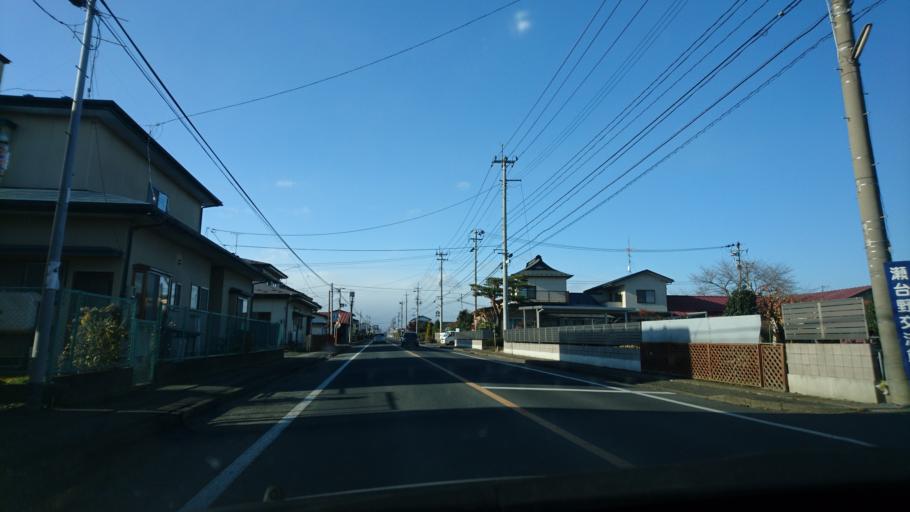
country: JP
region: Iwate
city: Mizusawa
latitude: 39.1264
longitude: 141.1609
